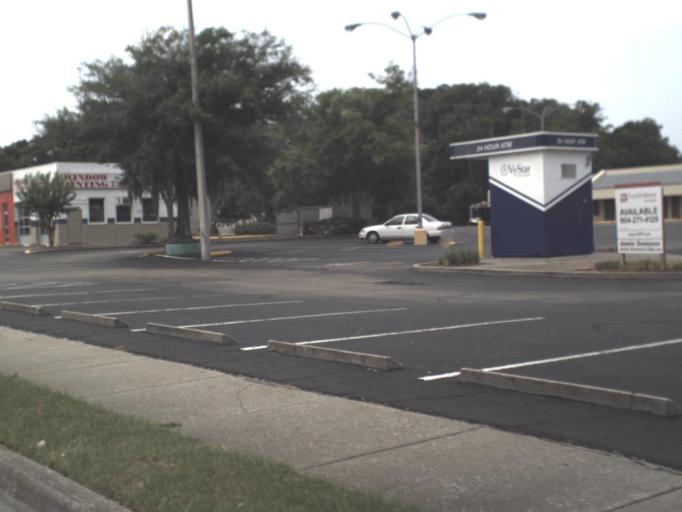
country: US
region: Florida
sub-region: Clay County
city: Orange Park
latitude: 30.1715
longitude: -81.7014
